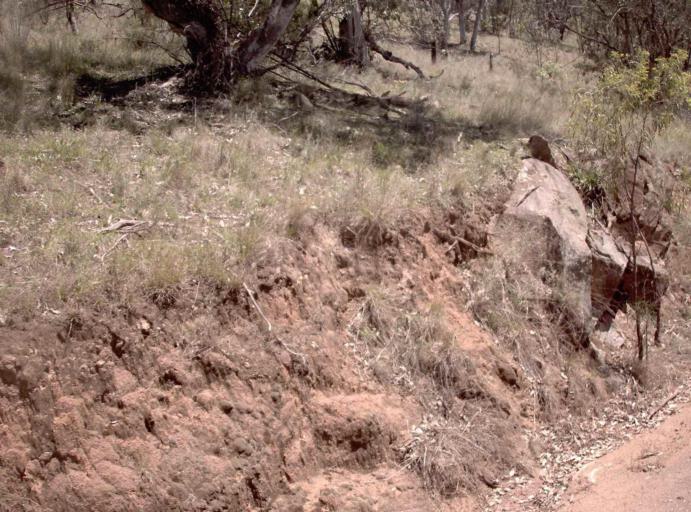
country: AU
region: New South Wales
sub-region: Snowy River
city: Jindabyne
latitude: -36.9371
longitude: 148.3441
